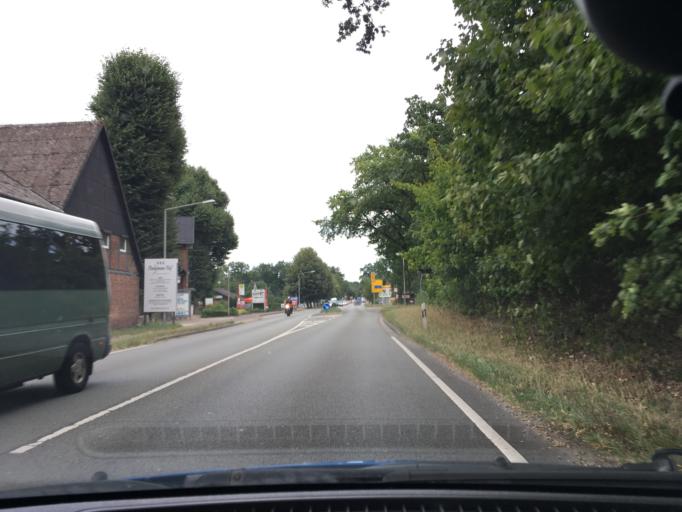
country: DE
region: Lower Saxony
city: Neu Wulmstorf
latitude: 53.4514
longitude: 9.7459
